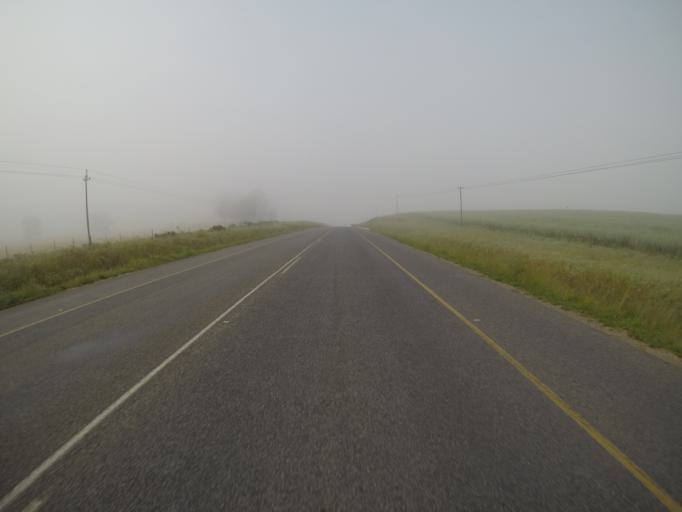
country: ZA
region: Western Cape
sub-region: City of Cape Town
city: Kraaifontein
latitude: -33.6794
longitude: 18.7060
